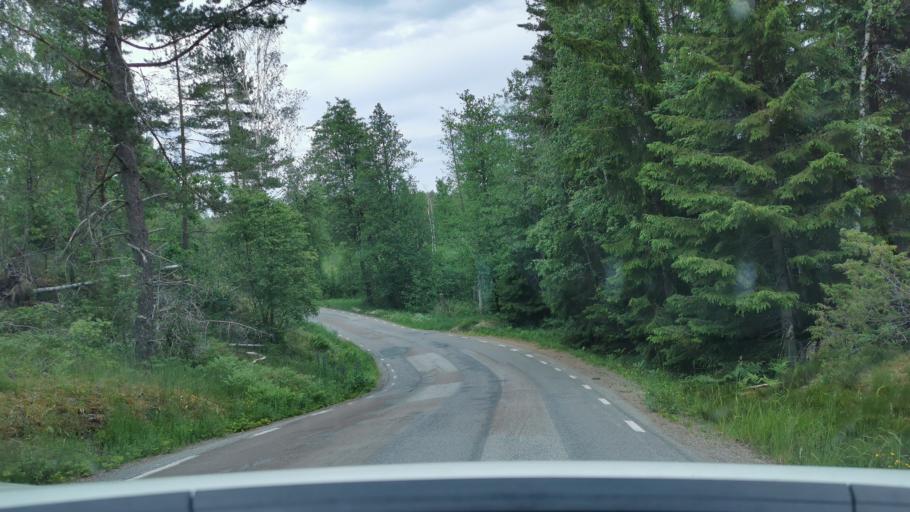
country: SE
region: Vaestra Goetaland
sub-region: Bengtsfors Kommun
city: Dals Langed
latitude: 58.8585
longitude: 12.4030
